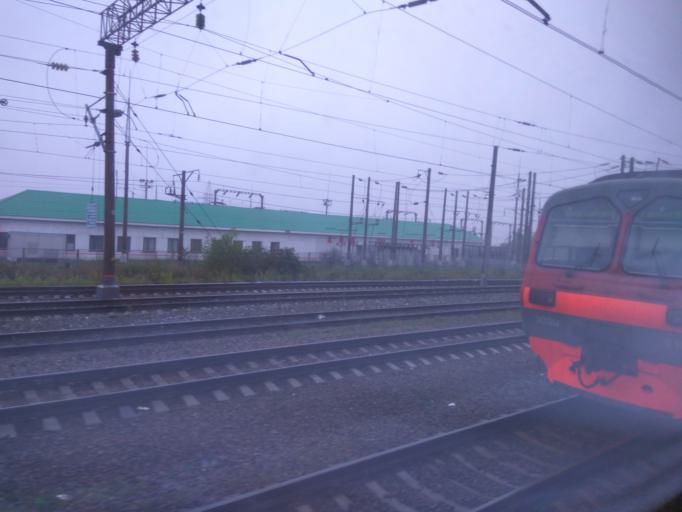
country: RU
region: Moskovskaya
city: Uzunovo
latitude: 54.5510
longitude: 38.6203
